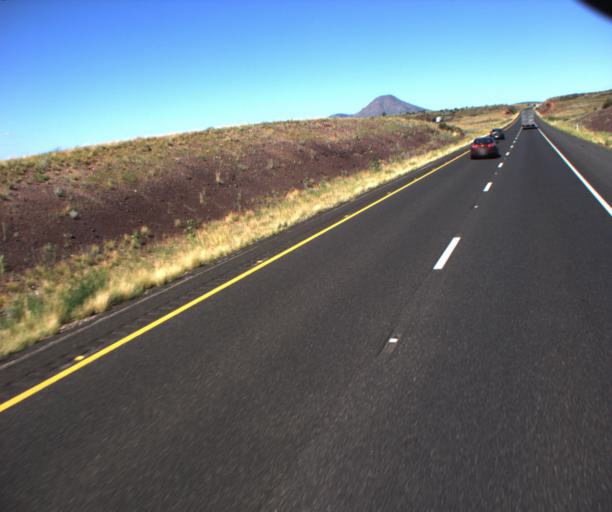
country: US
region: Arizona
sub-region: Yavapai County
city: Paulden
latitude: 35.2360
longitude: -112.6375
